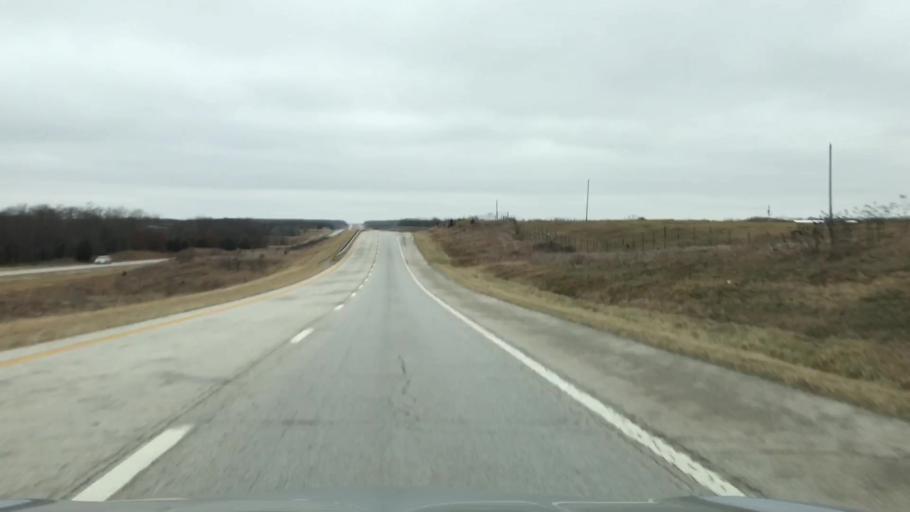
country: US
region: Missouri
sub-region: Linn County
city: Marceline
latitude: 39.7592
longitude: -92.8832
